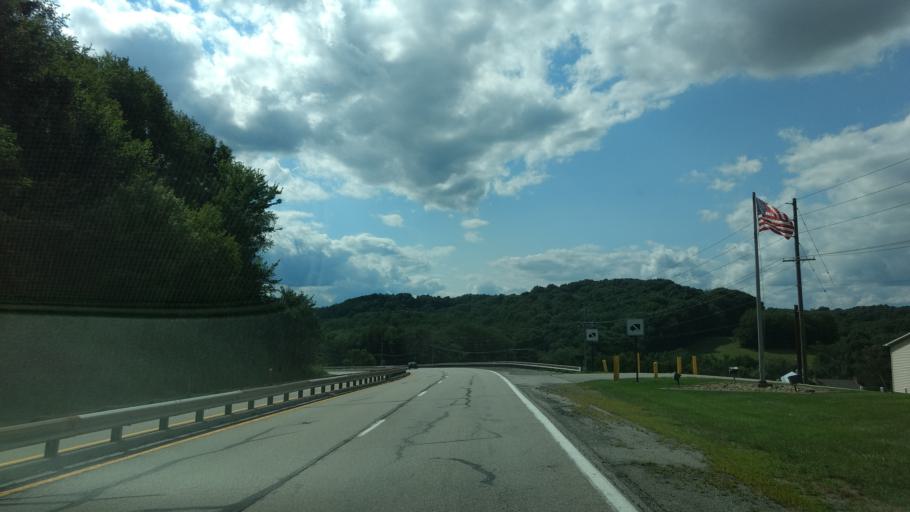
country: US
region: Pennsylvania
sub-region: Armstrong County
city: Apollo
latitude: 40.5328
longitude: -79.6179
